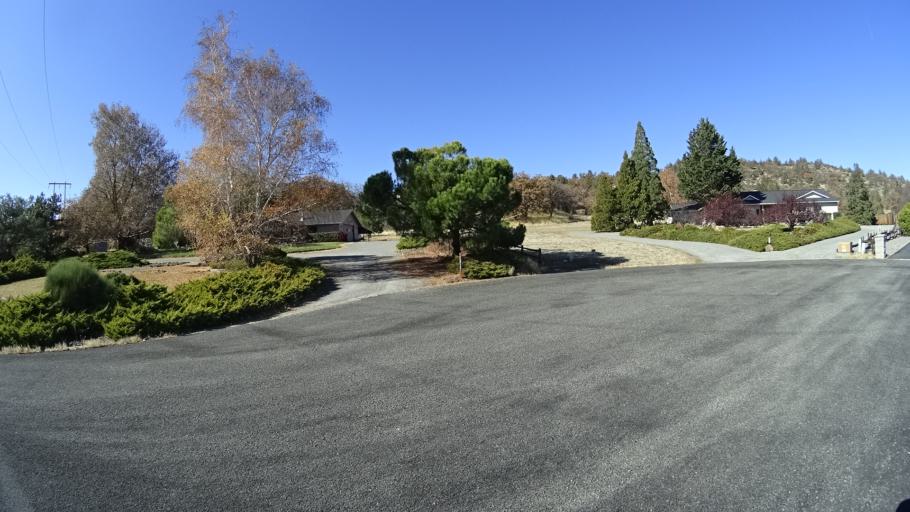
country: US
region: California
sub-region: Siskiyou County
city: Yreka
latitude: 41.7452
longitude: -122.6014
